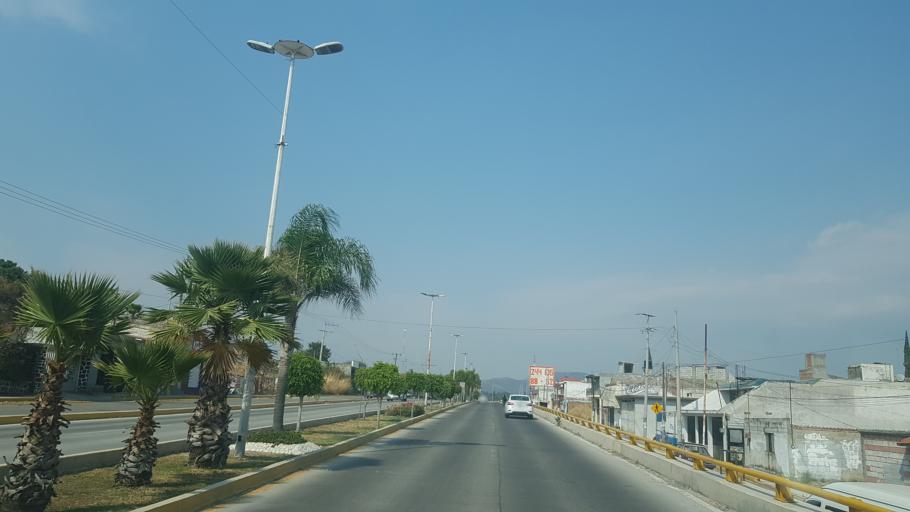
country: MX
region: Puebla
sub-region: Atlixco
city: El Encanto del Cerril
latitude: 18.9210
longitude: -98.4168
